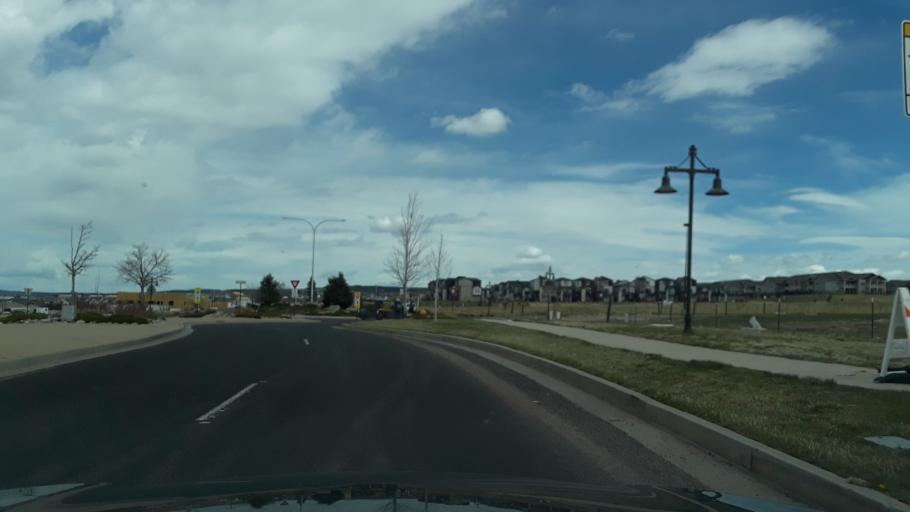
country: US
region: Colorado
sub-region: El Paso County
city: Gleneagle
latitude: 38.9919
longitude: -104.8034
